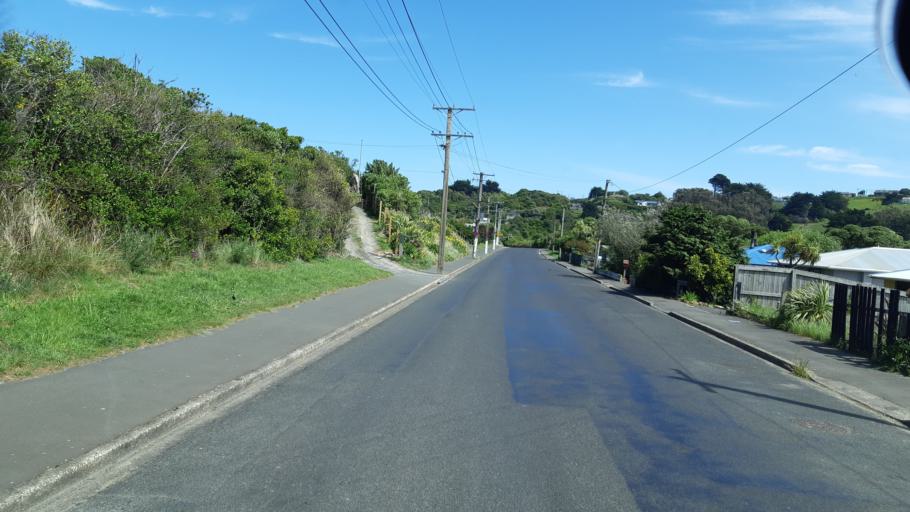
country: NZ
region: Otago
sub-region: Dunedin City
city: Dunedin
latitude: -45.9036
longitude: 170.5455
